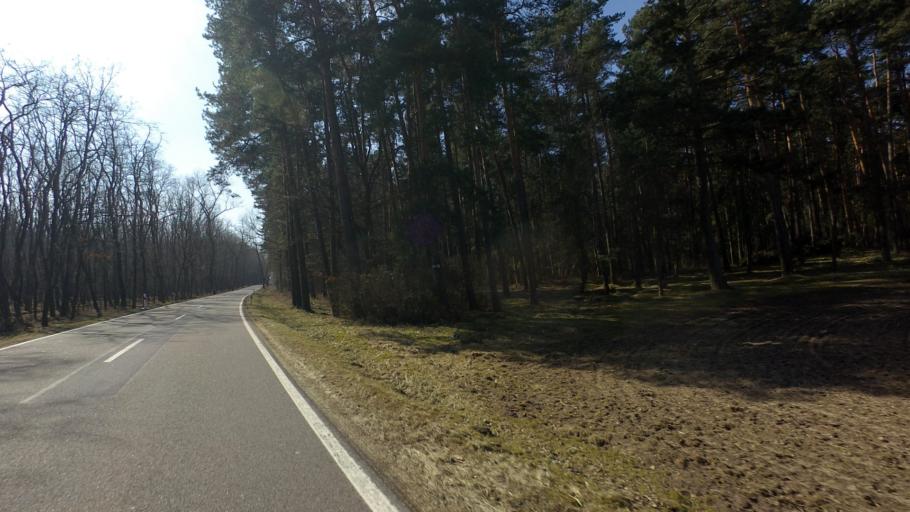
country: DE
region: Saxony-Anhalt
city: Nudersdorf
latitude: 51.9892
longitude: 12.5837
